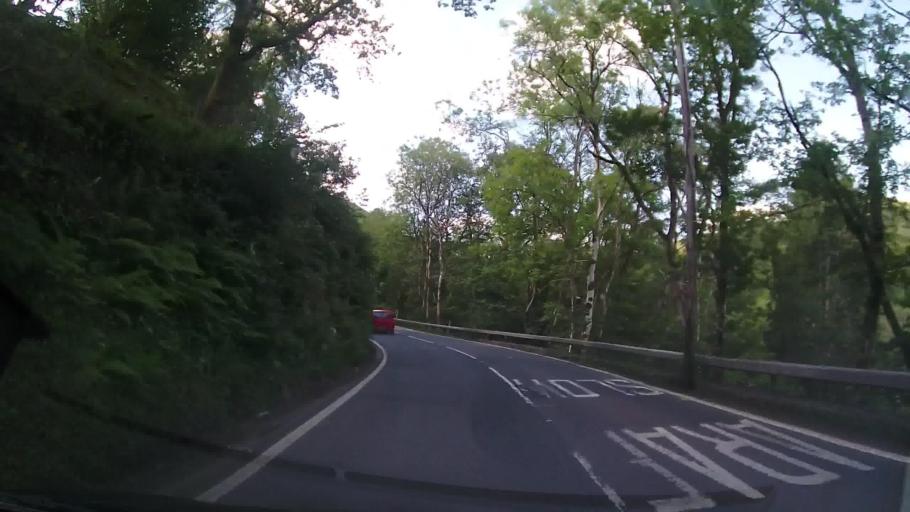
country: GB
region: Wales
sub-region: Gwynedd
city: Bala
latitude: 52.6990
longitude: -3.6235
